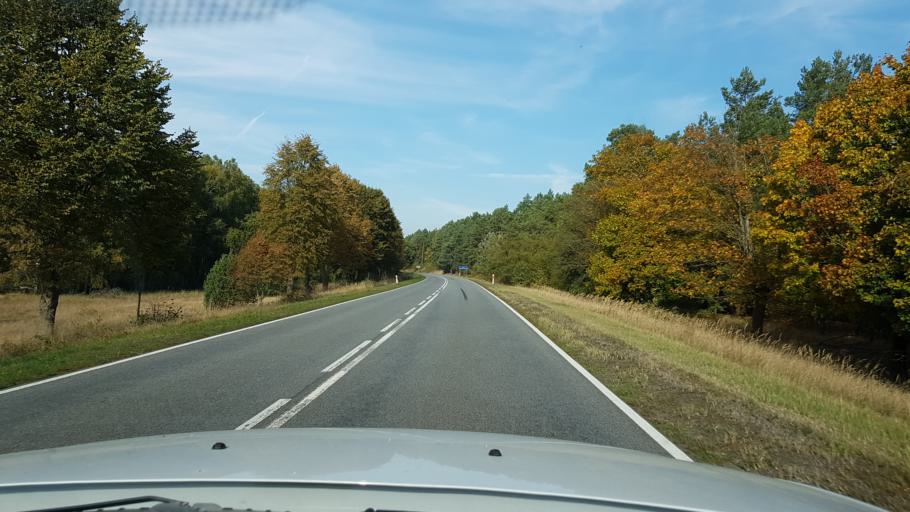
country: PL
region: West Pomeranian Voivodeship
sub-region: Powiat mysliborski
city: Nowogrodek Pomorski
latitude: 52.9163
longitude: 14.9679
